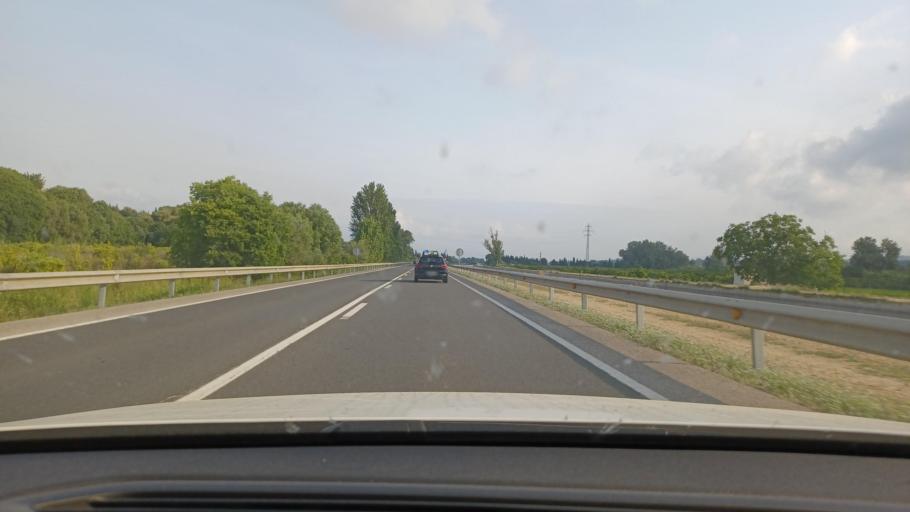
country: ES
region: Catalonia
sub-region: Provincia de Tarragona
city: Masdenverge
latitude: 40.7604
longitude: 0.5349
